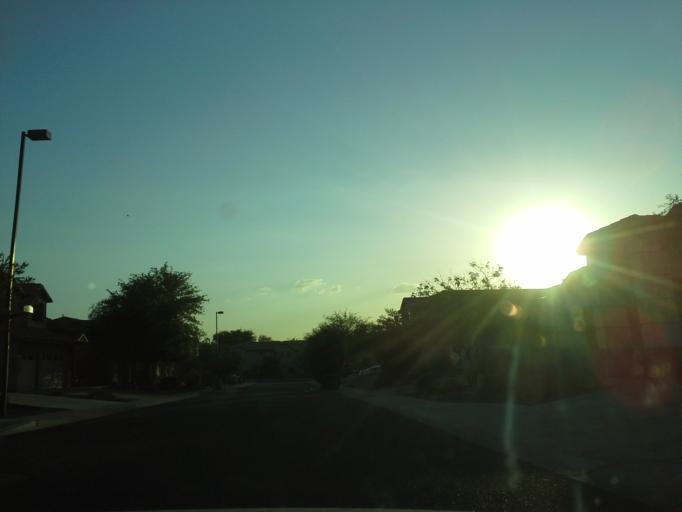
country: US
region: Arizona
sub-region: Maricopa County
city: Anthem
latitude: 33.7536
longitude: -112.1032
